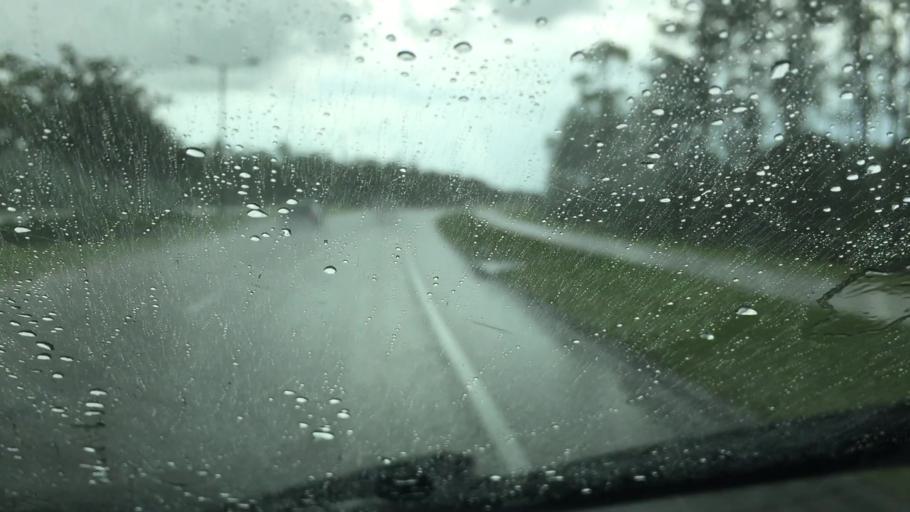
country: US
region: Florida
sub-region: Lee County
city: Three Oaks
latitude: 26.4583
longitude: -81.7821
